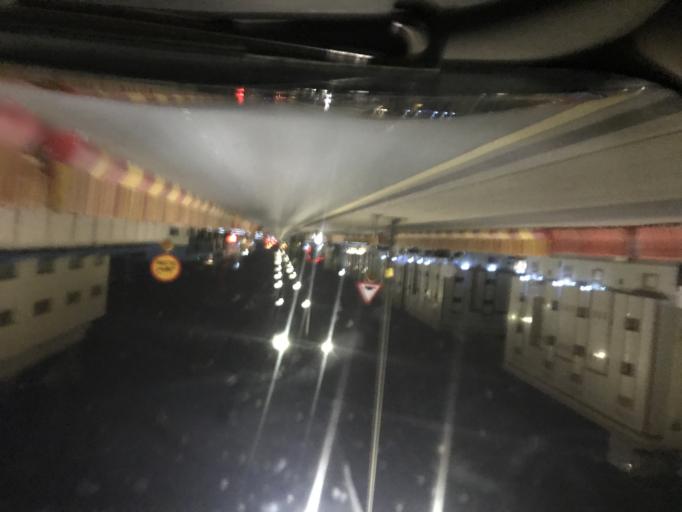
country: SA
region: Ar Riyad
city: Riyadh
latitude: 24.7985
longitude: 46.7088
